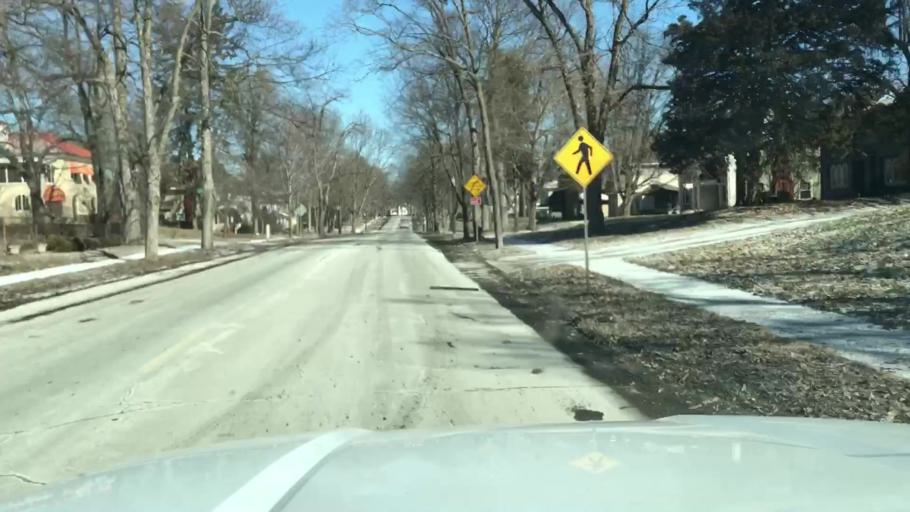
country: US
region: Missouri
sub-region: Buchanan County
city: Saint Joseph
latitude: 39.7811
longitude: -94.8248
